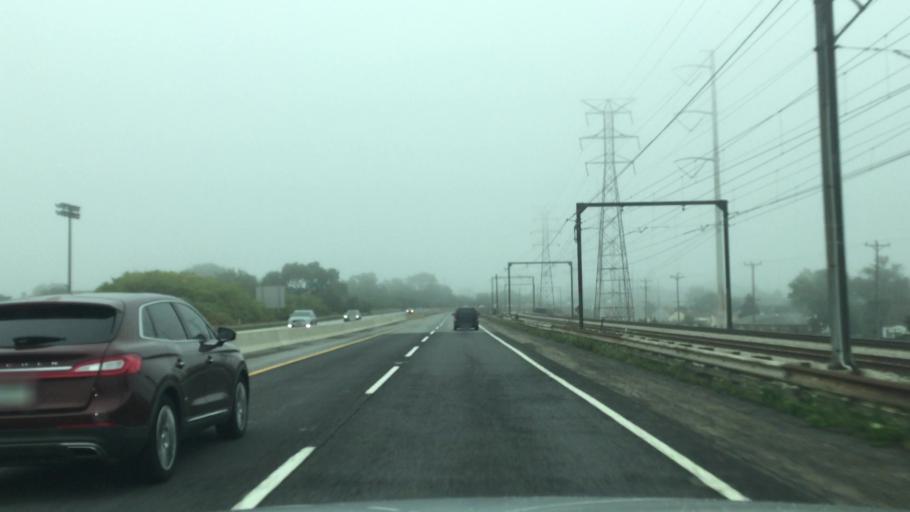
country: US
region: Illinois
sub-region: Cook County
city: Calumet City
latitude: 41.6286
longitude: -87.4954
